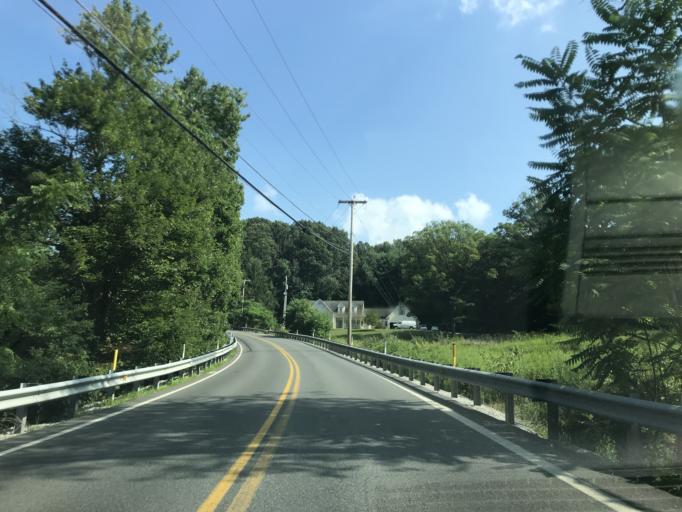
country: US
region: Pennsylvania
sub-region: York County
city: Glen Rock
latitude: 39.7510
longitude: -76.8087
